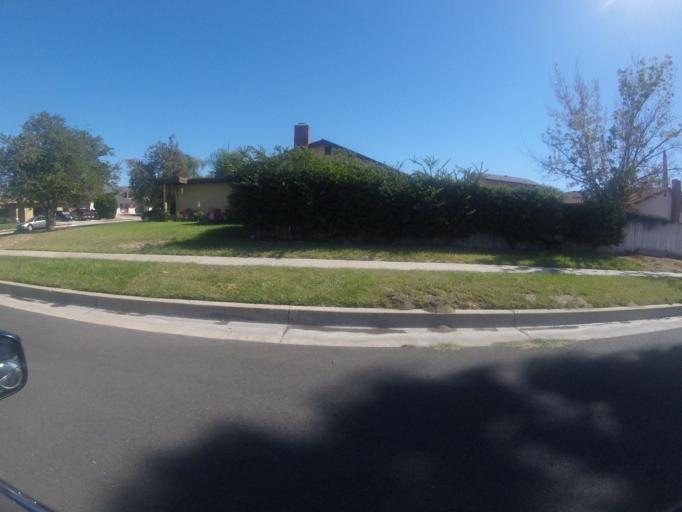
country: US
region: California
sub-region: San Bernardino County
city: Redlands
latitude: 34.0750
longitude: -117.1727
